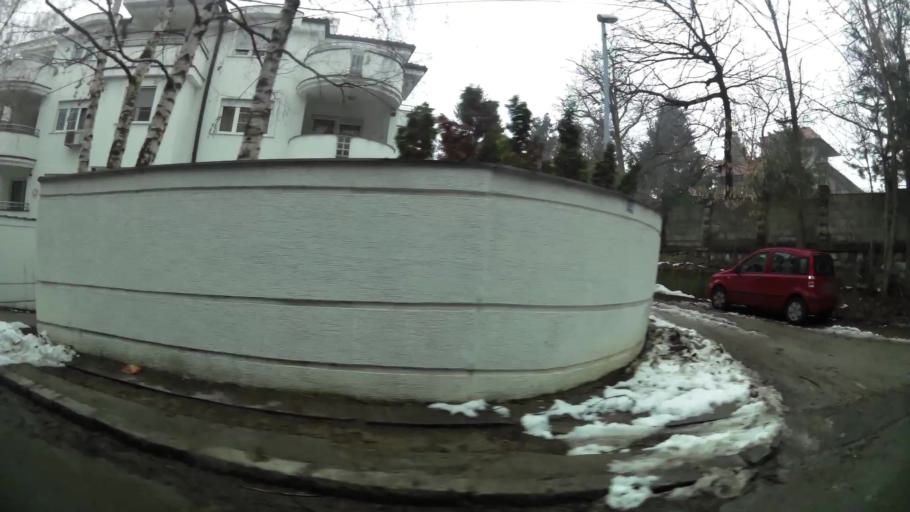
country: RS
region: Central Serbia
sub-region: Belgrade
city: Cukarica
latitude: 44.7894
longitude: 20.4318
